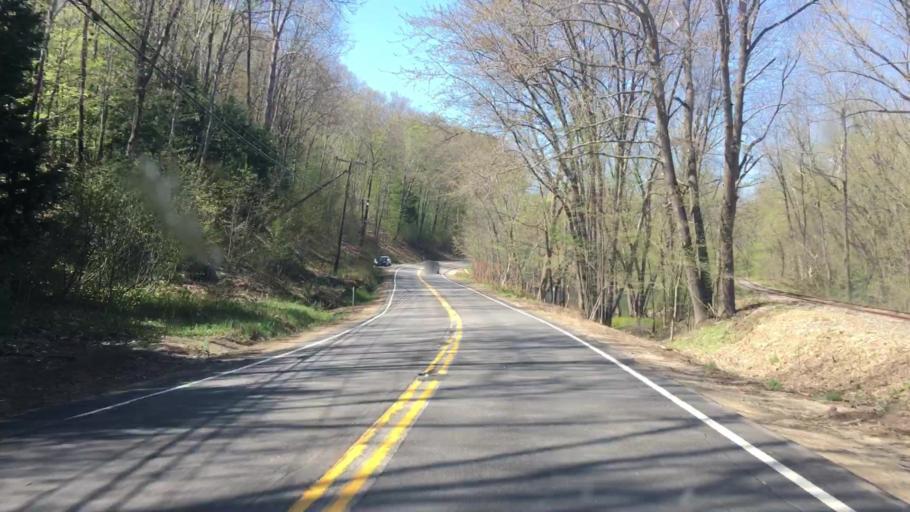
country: US
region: New Hampshire
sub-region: Grafton County
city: Plymouth
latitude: 43.7430
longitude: -71.6793
